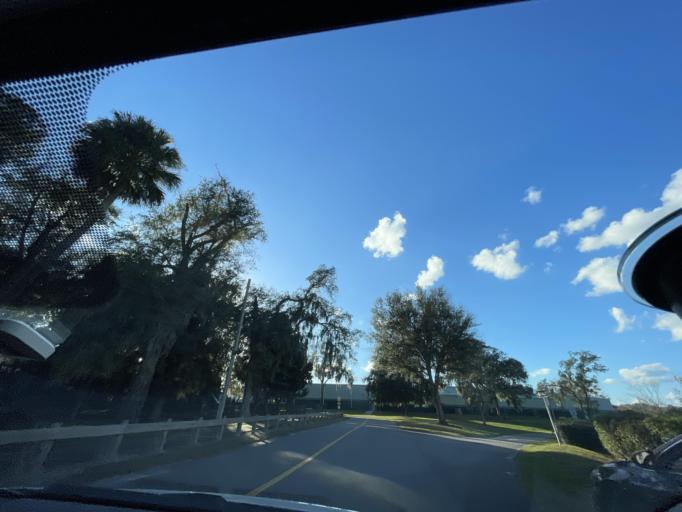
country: US
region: Florida
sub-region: Volusia County
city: Ormond Beach
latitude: 29.2871
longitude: -81.0854
